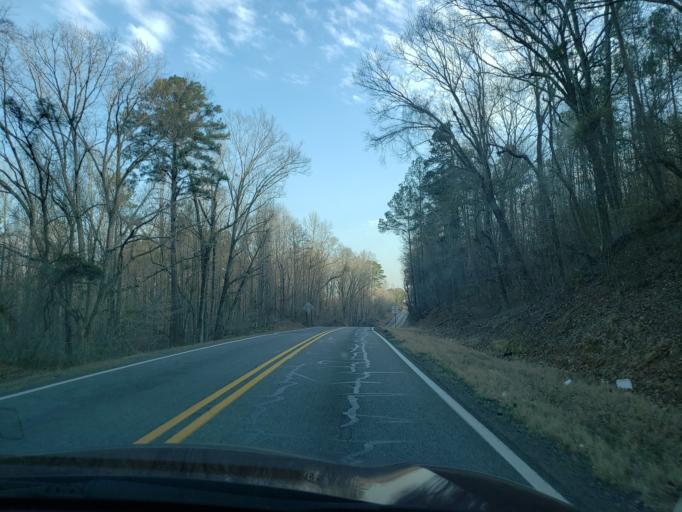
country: US
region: Alabama
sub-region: Hale County
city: Greensboro
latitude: 32.8106
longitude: -87.5951
